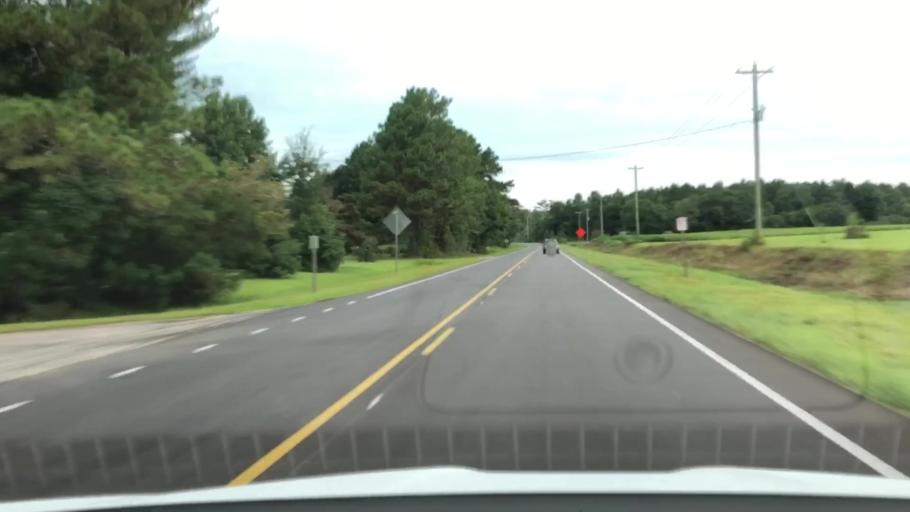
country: US
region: North Carolina
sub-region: Jones County
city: Maysville
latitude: 34.8678
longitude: -77.1934
